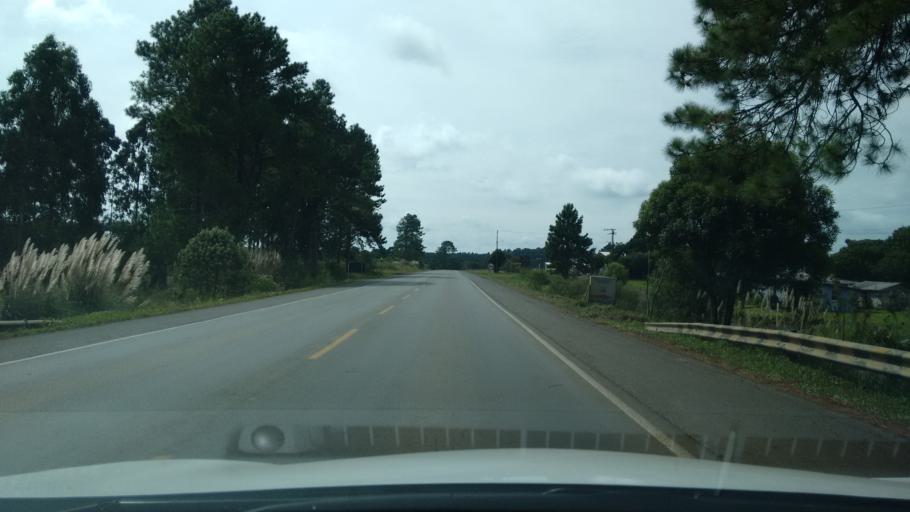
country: BR
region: Santa Catarina
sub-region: Curitibanos
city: Curitibanos
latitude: -27.3021
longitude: -50.4195
